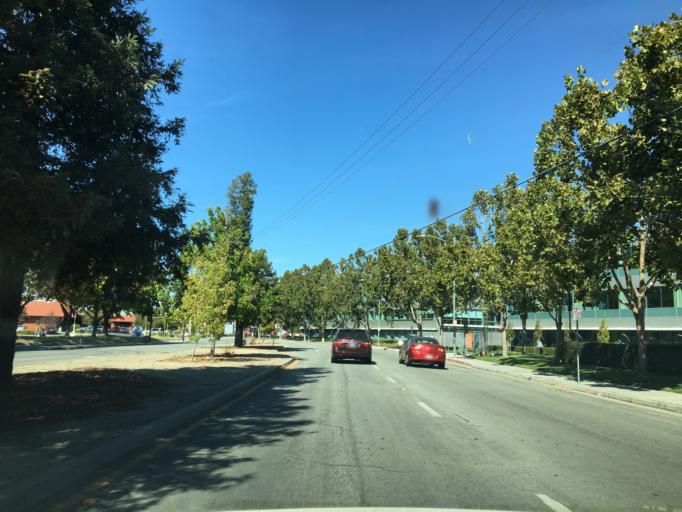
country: US
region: California
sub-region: Santa Clara County
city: Buena Vista
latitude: 37.3169
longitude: -121.9141
